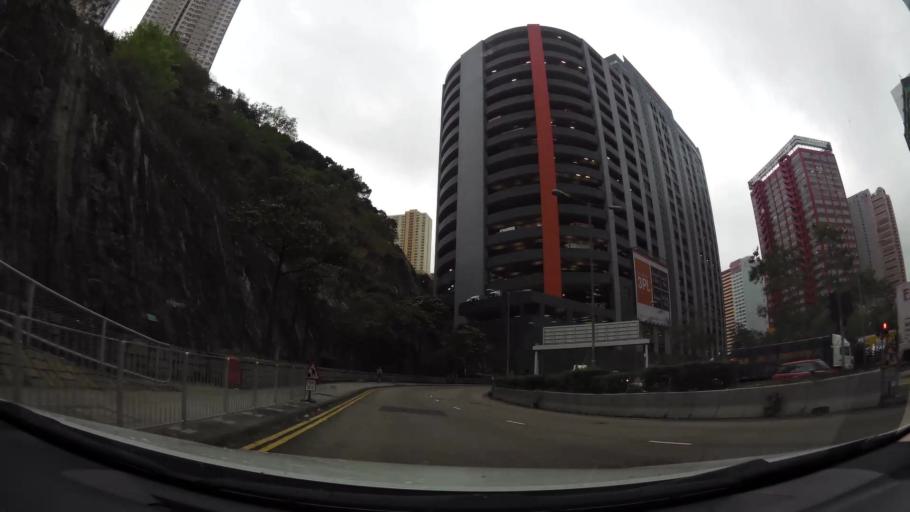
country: HK
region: Tsuen Wan
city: Tsuen Wan
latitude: 22.3653
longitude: 114.1212
